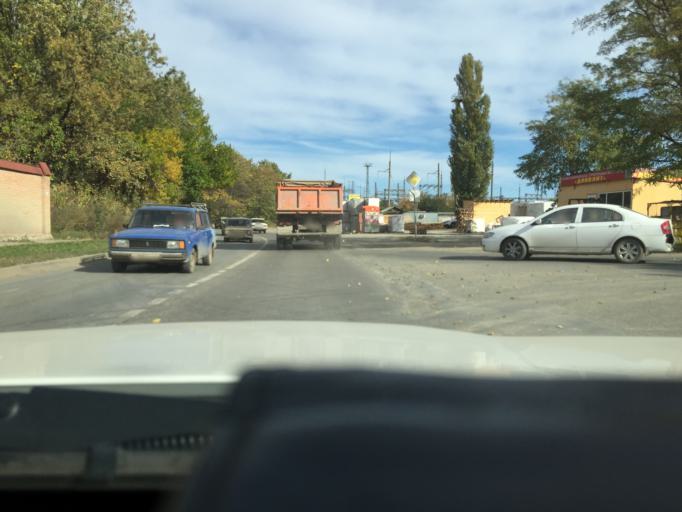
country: RU
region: Rostov
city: Imeni Chkalova
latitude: 47.2894
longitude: 39.8037
